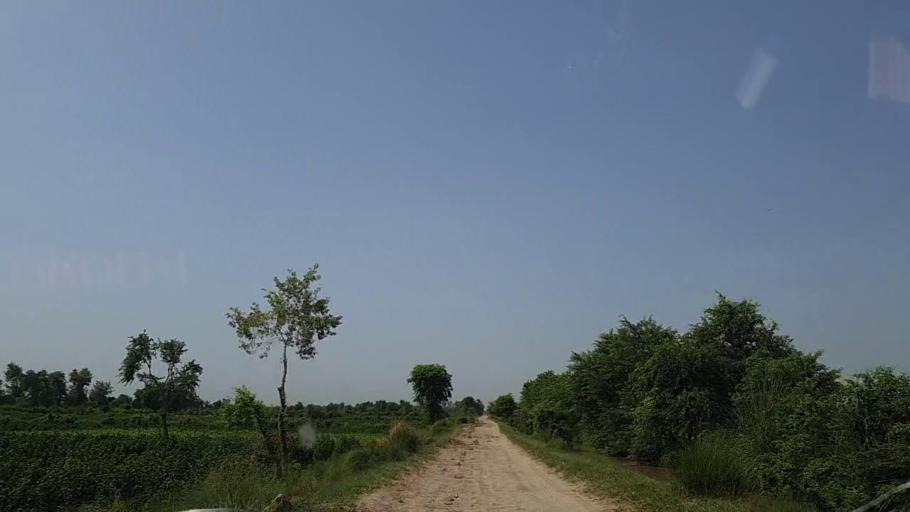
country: PK
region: Sindh
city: Naushahro Firoz
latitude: 26.8646
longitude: 68.0313
